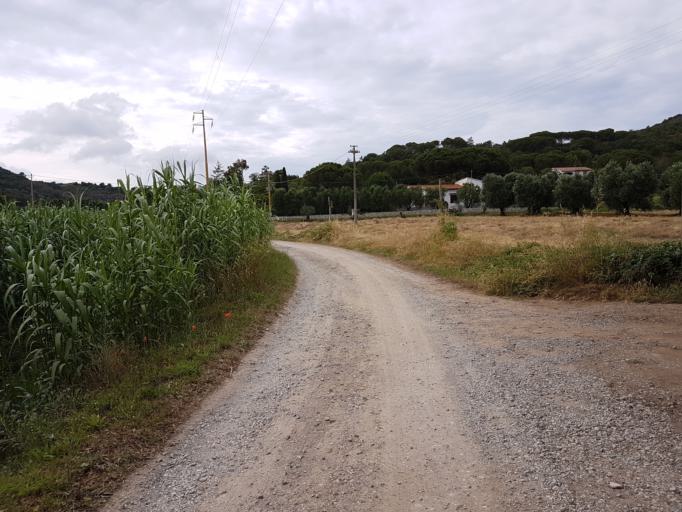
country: IT
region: Tuscany
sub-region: Provincia di Livorno
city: Capoliveri
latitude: 42.7780
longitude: 10.3497
